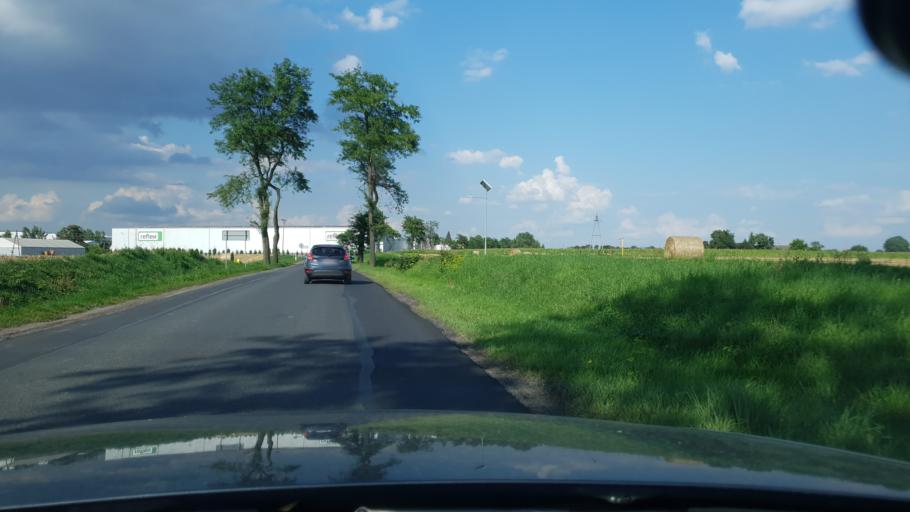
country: PL
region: Kujawsko-Pomorskie
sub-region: Powiat wabrzeski
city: Wabrzezno
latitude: 53.2725
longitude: 18.9175
